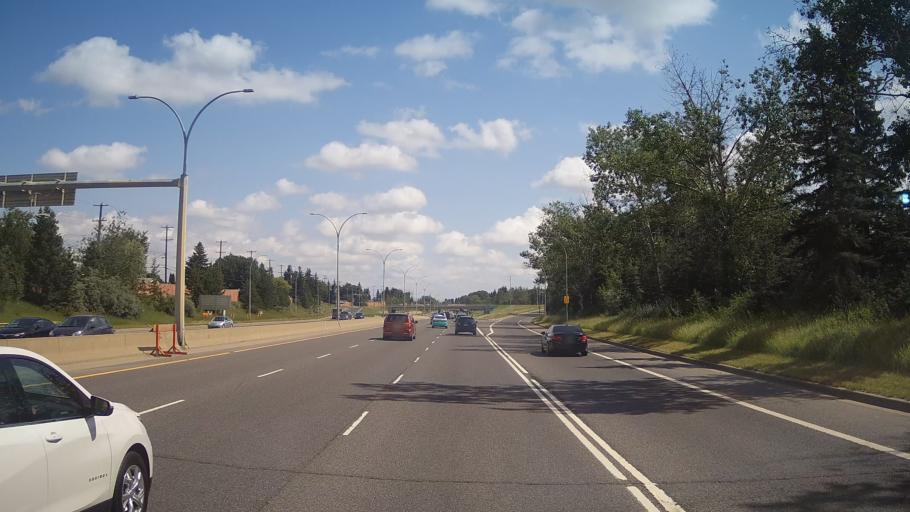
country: CA
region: Alberta
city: St. Albert
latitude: 53.5119
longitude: -113.6031
